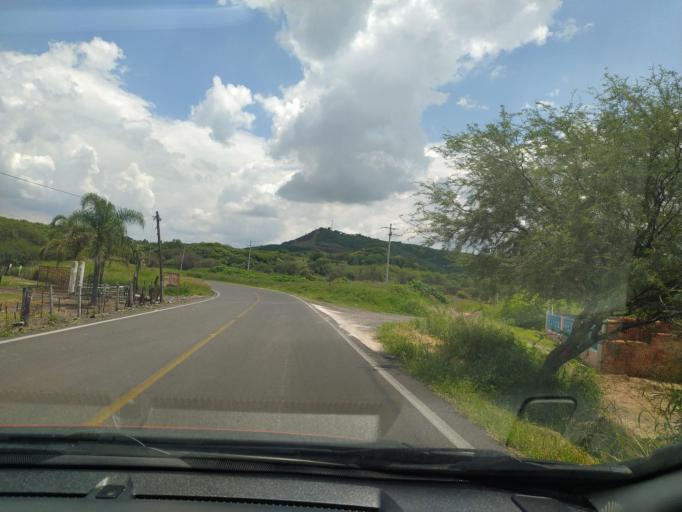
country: MX
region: Jalisco
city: Villa Corona
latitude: 20.4060
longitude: -103.6844
